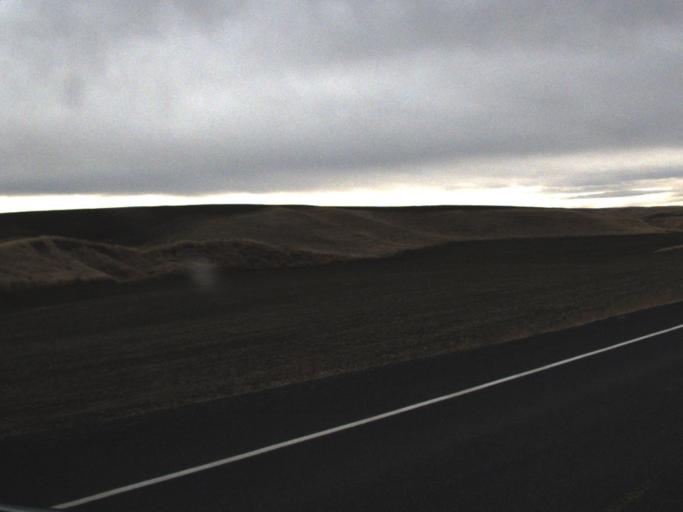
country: US
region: Washington
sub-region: Garfield County
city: Pomeroy
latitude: 46.7907
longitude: -117.8954
